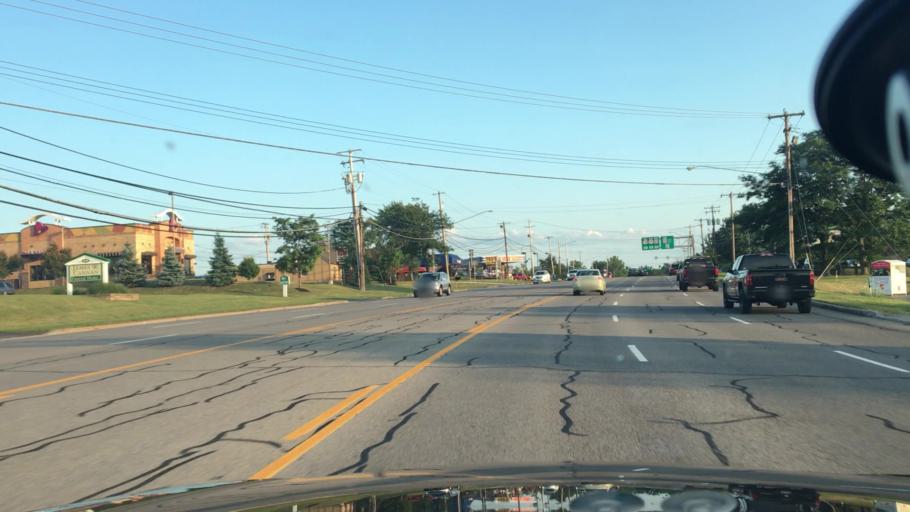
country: US
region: New York
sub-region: Erie County
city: Orchard Park
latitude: 42.7995
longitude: -78.7517
